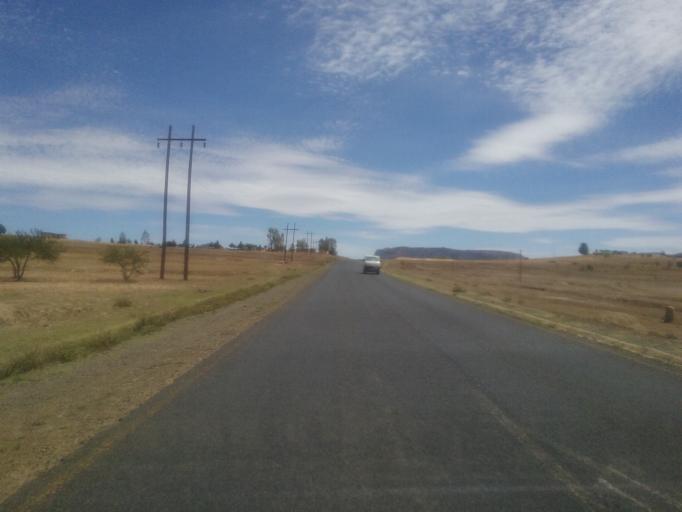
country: LS
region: Mafeteng
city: Mafeteng
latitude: -29.9846
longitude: 27.3256
